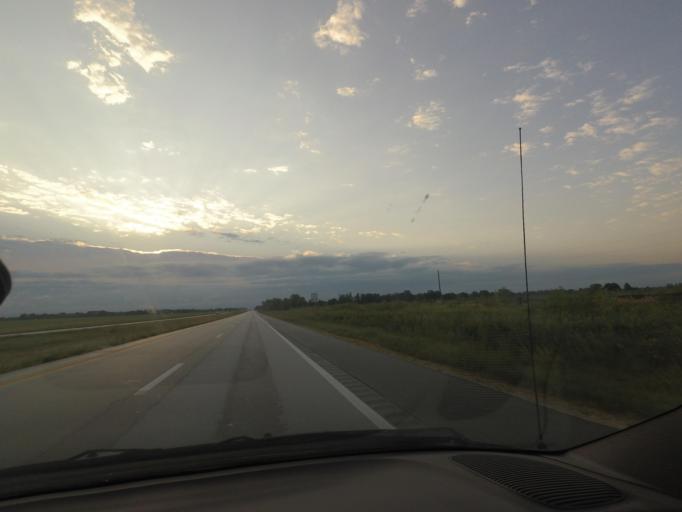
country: US
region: Missouri
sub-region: Shelby County
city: Shelbina
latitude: 39.7269
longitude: -92.1820
